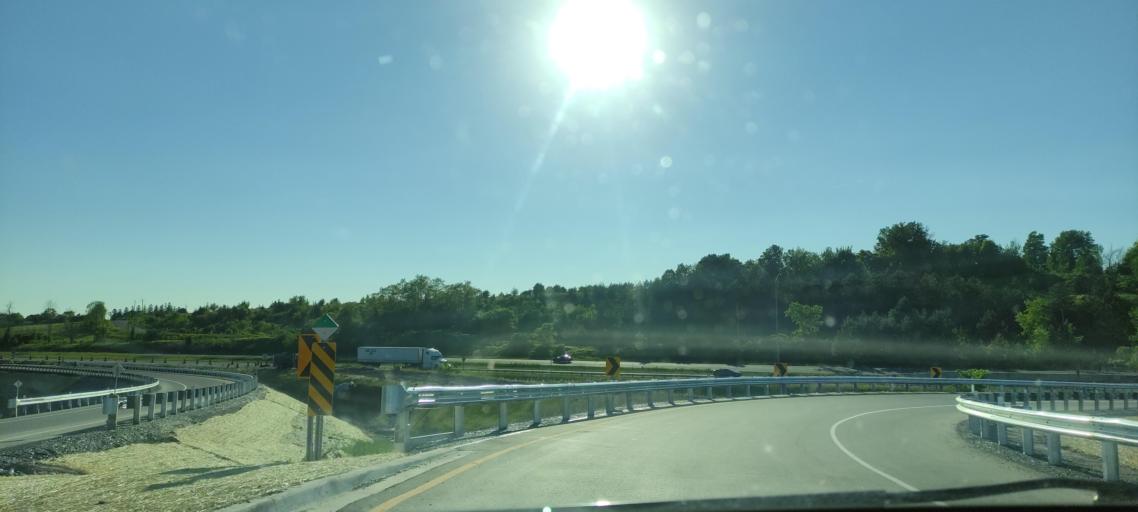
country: CA
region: Ontario
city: Quinte West
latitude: 44.0729
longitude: -77.7692
